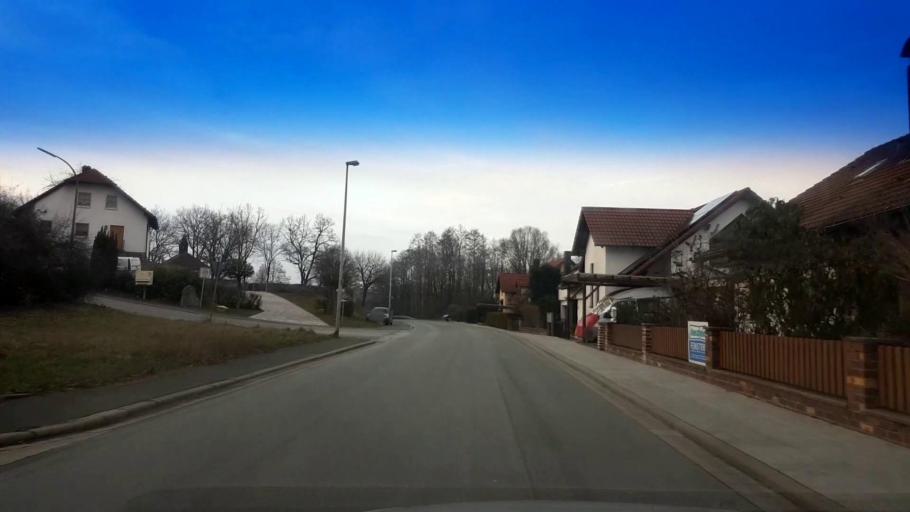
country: DE
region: Bavaria
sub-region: Upper Franconia
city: Altendorf
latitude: 49.7952
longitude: 10.9960
